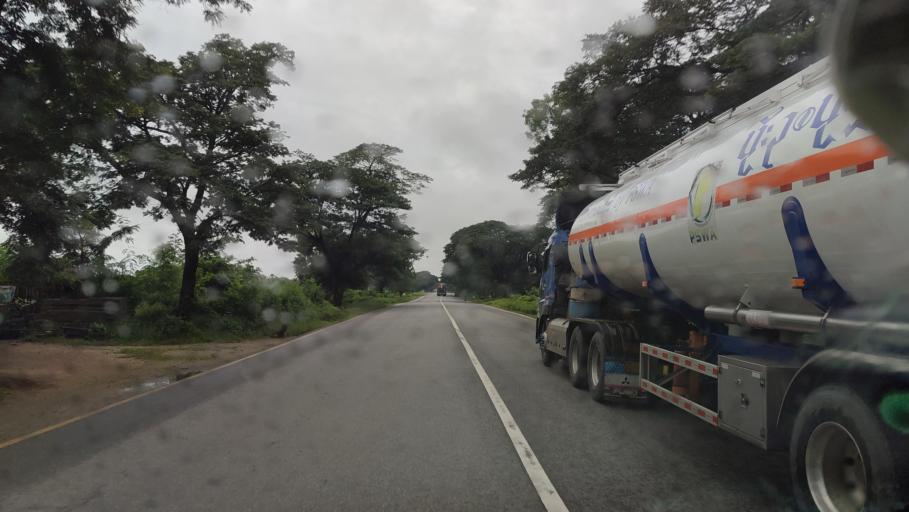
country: MM
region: Mandalay
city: Pyinmana
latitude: 19.9601
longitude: 96.2537
